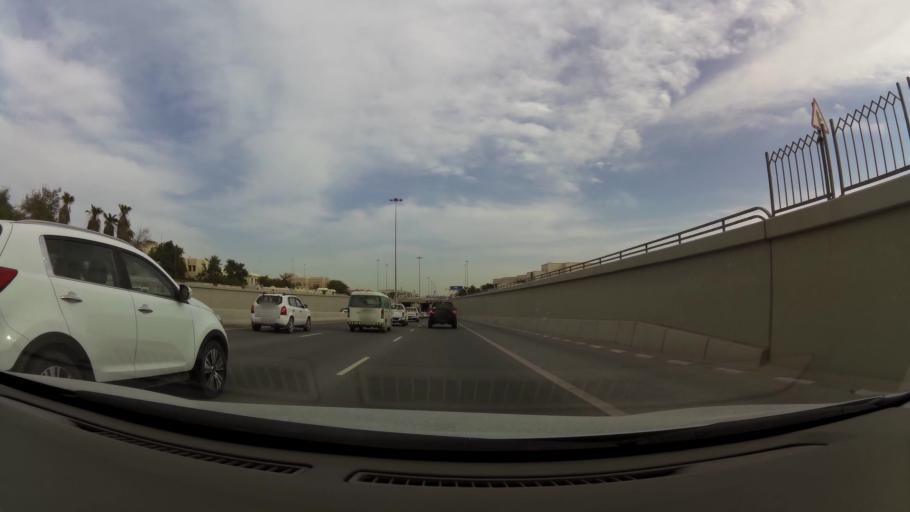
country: QA
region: Baladiyat ad Dawhah
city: Doha
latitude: 25.2783
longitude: 51.4871
